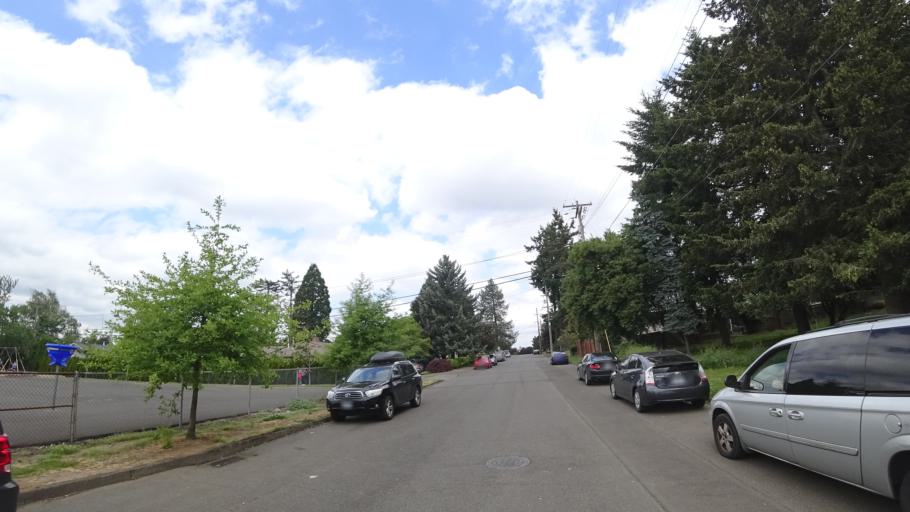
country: US
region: Oregon
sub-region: Multnomah County
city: Lents
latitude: 45.5095
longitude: -122.5538
